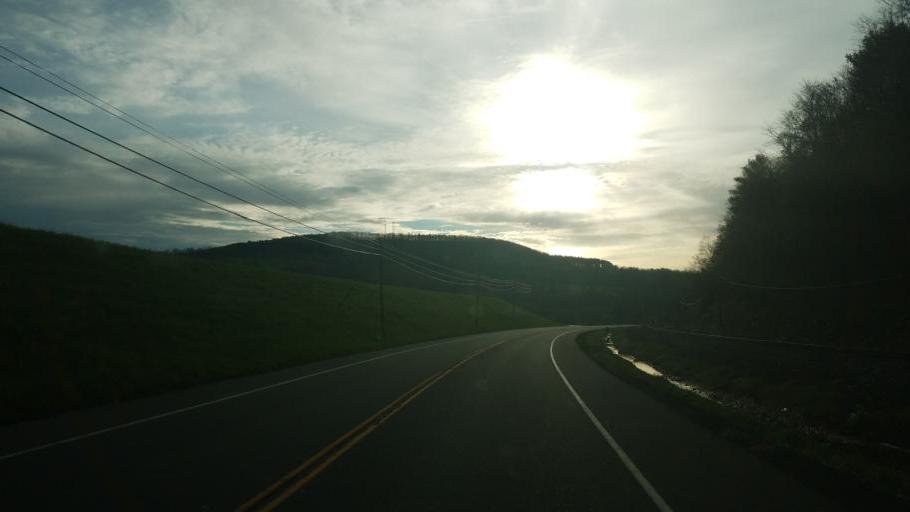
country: US
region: New York
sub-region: Steuben County
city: Hornell
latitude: 42.3443
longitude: -77.7099
